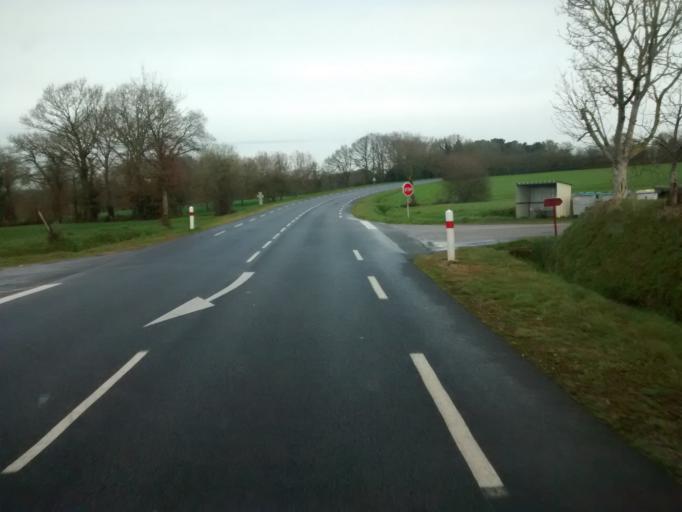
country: FR
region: Brittany
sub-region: Departement du Morbihan
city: Malestroit
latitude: 47.8321
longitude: -2.3901
